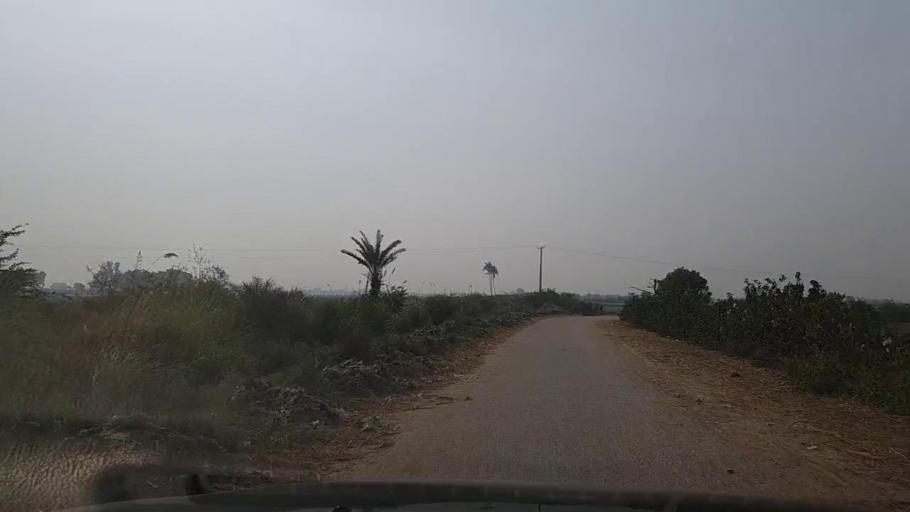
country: PK
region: Sindh
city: Mirpur Sakro
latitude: 24.5478
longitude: 67.8342
